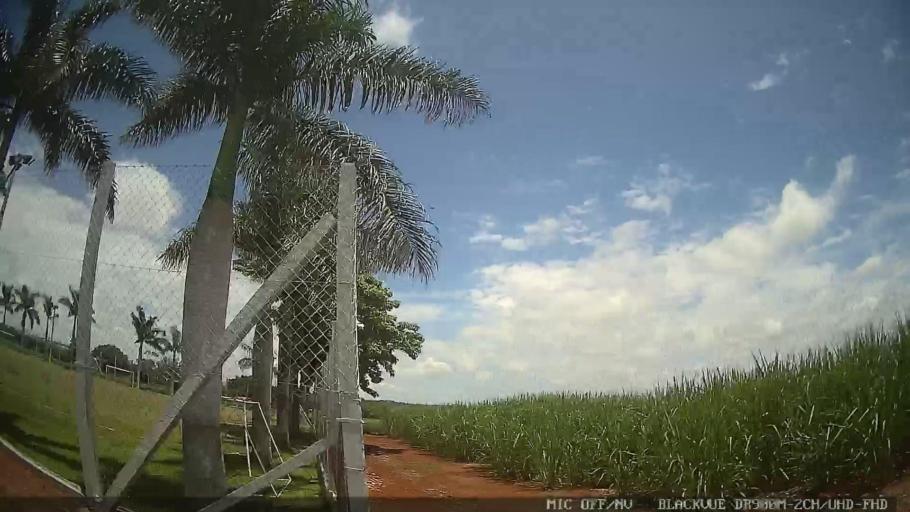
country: BR
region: Sao Paulo
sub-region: Laranjal Paulista
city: Laranjal Paulista
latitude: -23.0317
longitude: -47.8586
